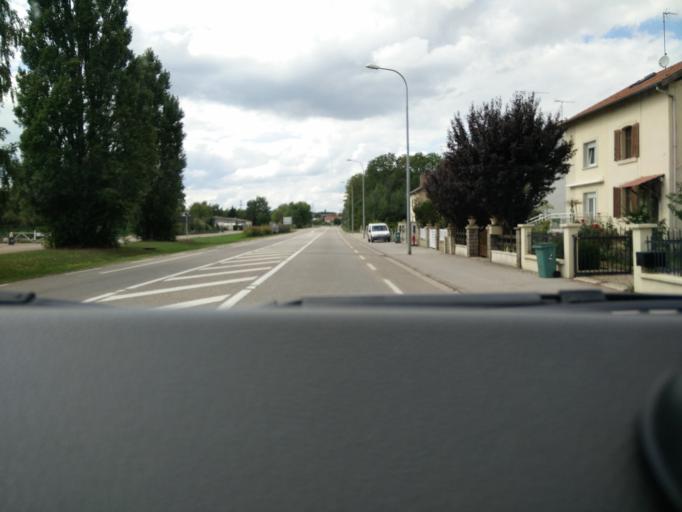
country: FR
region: Lorraine
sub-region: Departement de Meurthe-et-Moselle
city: Art-sur-Meurthe
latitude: 48.6424
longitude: 6.2591
